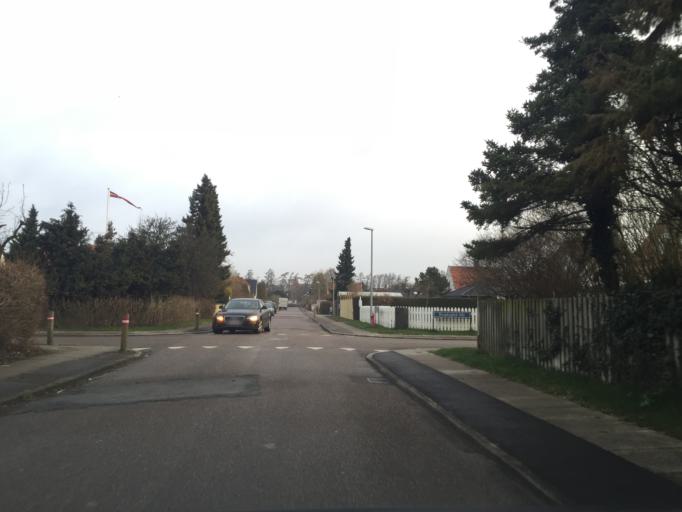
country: DK
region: Capital Region
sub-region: Tarnby Kommune
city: Tarnby
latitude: 55.6247
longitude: 12.6068
